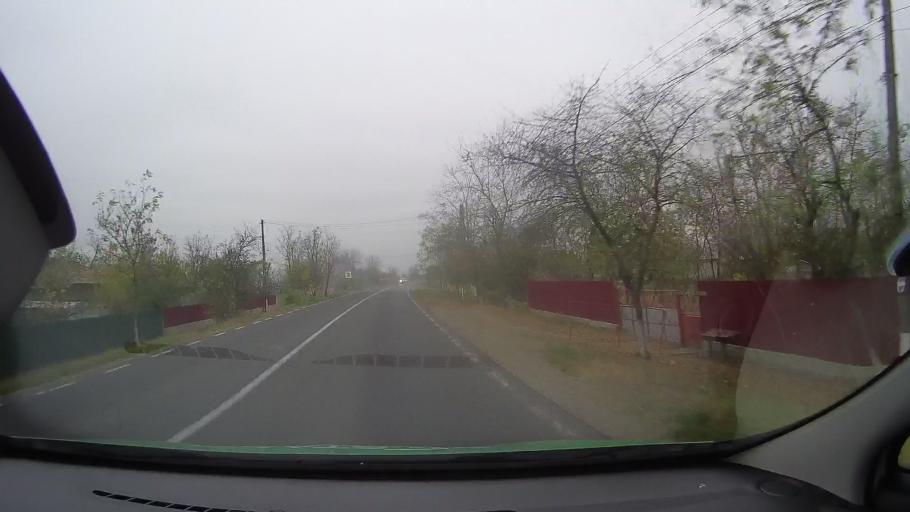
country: RO
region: Braila
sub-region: Comuna Baraganul
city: Baraganul
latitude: 44.8001
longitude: 27.5132
